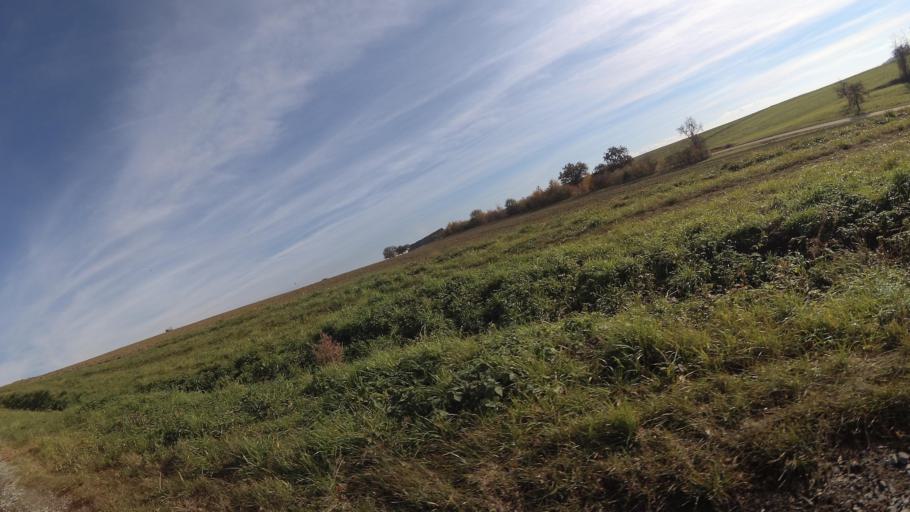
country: DE
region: Baden-Wuerttemberg
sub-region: Regierungsbezirk Stuttgart
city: Gundelsheim
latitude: 49.3025
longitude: 9.2080
